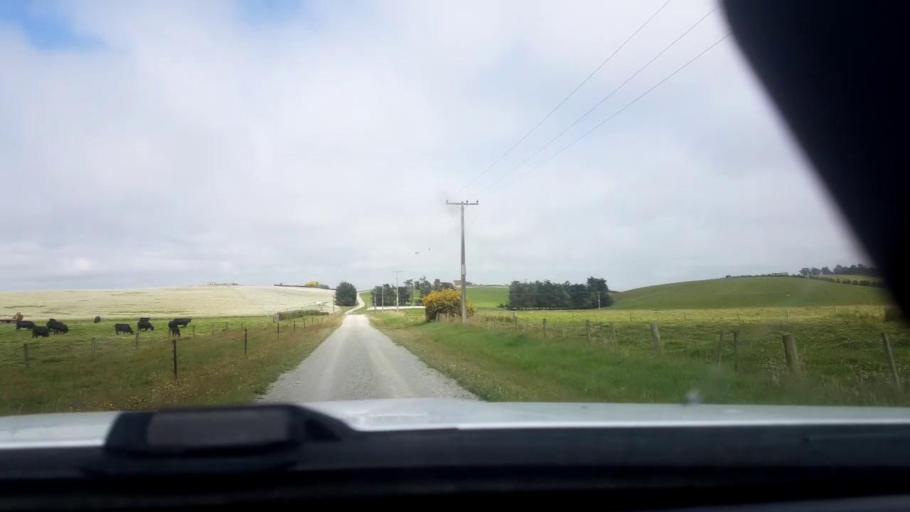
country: NZ
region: Canterbury
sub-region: Timaru District
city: Timaru
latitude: -44.3294
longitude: 171.2029
